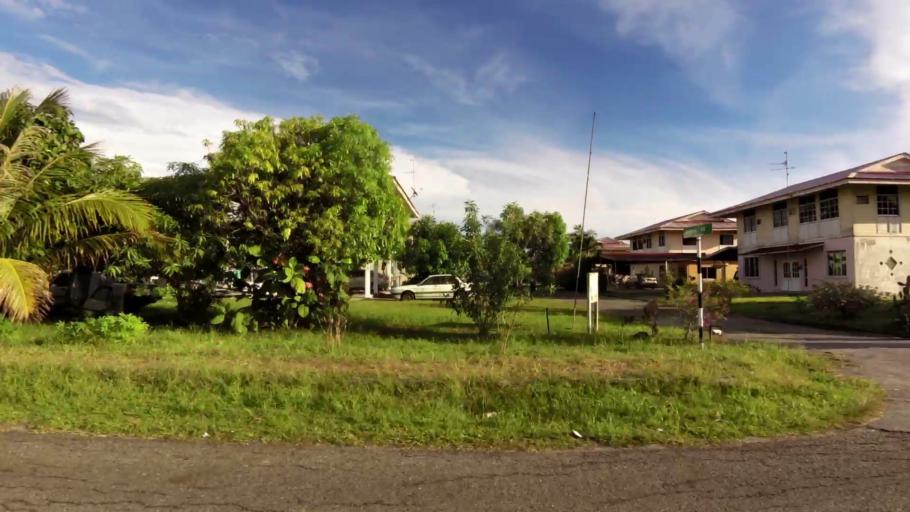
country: BN
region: Belait
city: Kuala Belait
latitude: 4.5784
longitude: 114.2239
